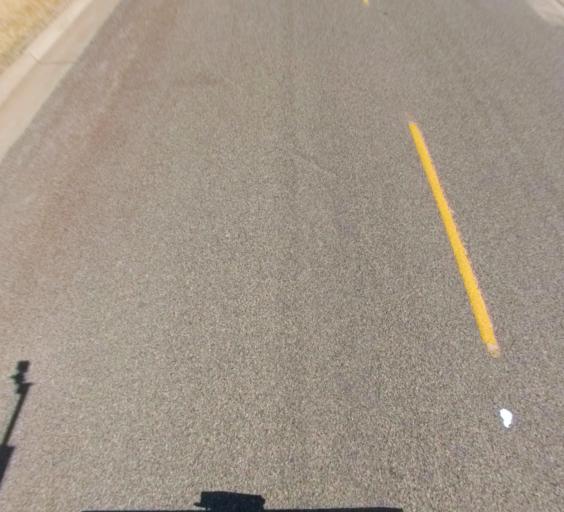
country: US
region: California
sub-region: Madera County
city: Bonadelle Ranchos-Madera Ranchos
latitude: 36.8987
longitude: -119.7968
